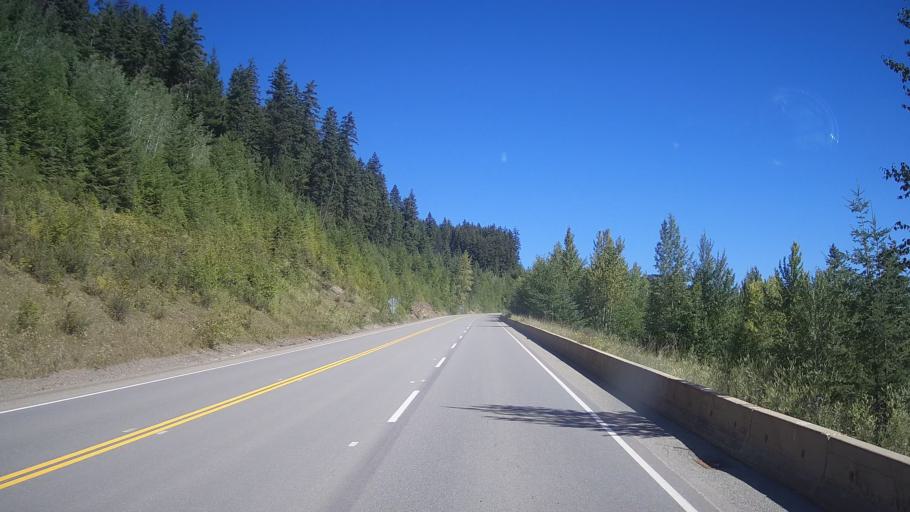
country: CA
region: British Columbia
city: Kamloops
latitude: 51.4727
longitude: -120.2564
